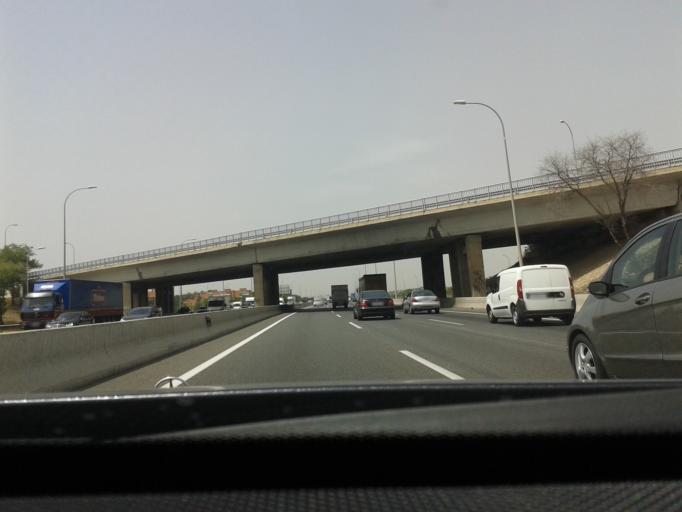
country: ES
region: Madrid
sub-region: Provincia de Madrid
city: Torrejon de Ardoz
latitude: 40.4667
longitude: -3.4549
